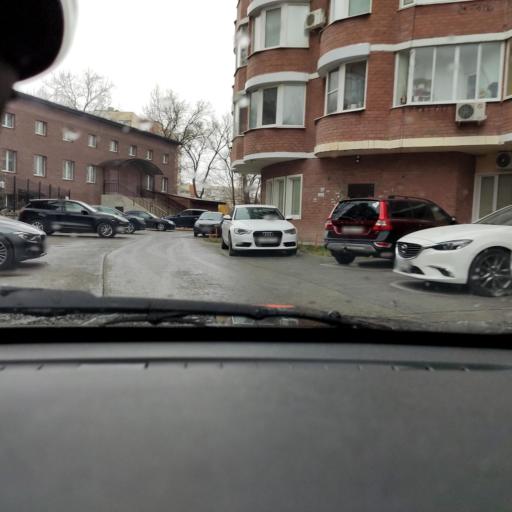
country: RU
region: Samara
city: Tol'yatti
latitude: 53.5366
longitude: 49.3620
